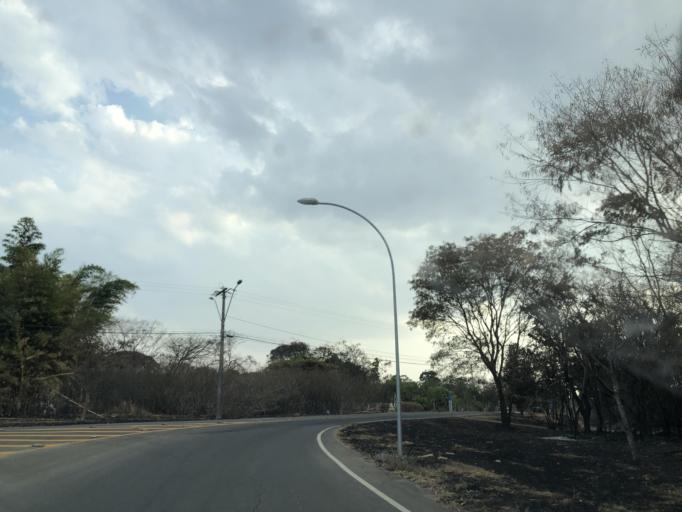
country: BR
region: Federal District
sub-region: Brasilia
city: Brasilia
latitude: -15.9385
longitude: -47.9752
